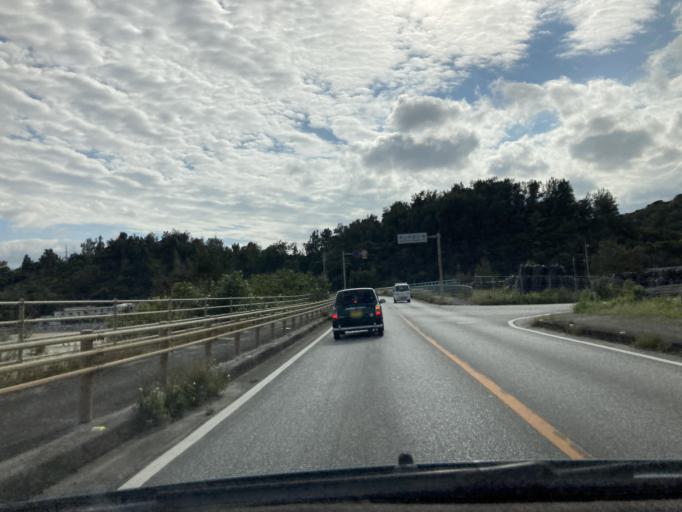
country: JP
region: Okinawa
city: Nago
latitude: 26.6356
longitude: 128.0030
